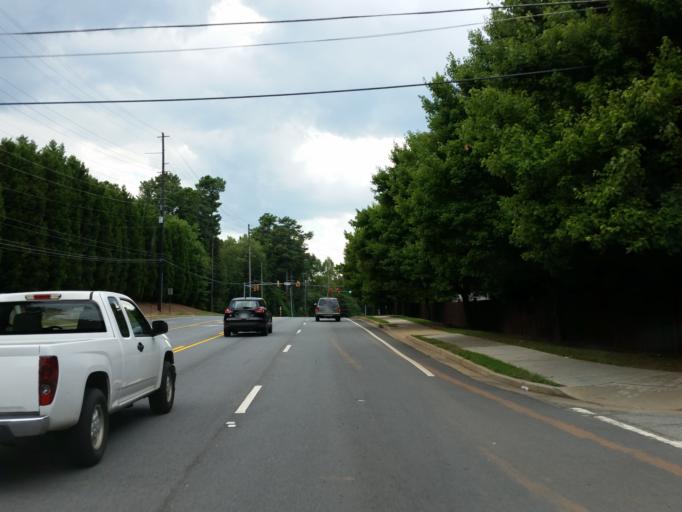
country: US
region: Georgia
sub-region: Cobb County
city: Vinings
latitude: 33.9150
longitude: -84.4708
